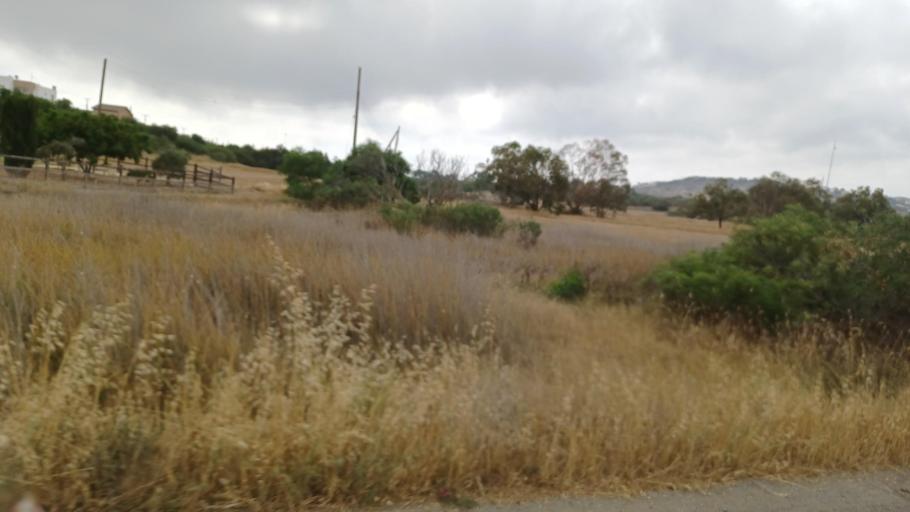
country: CY
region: Ammochostos
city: Protaras
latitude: 35.0177
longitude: 34.0199
